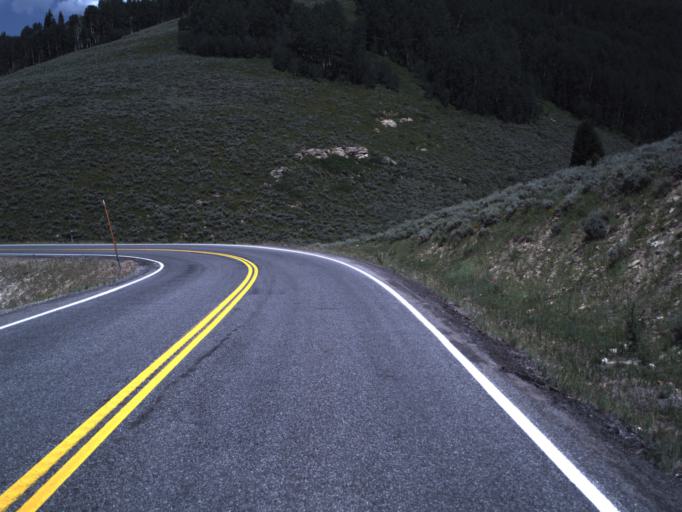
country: US
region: Utah
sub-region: Sanpete County
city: Fairview
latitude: 39.6862
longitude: -111.2447
